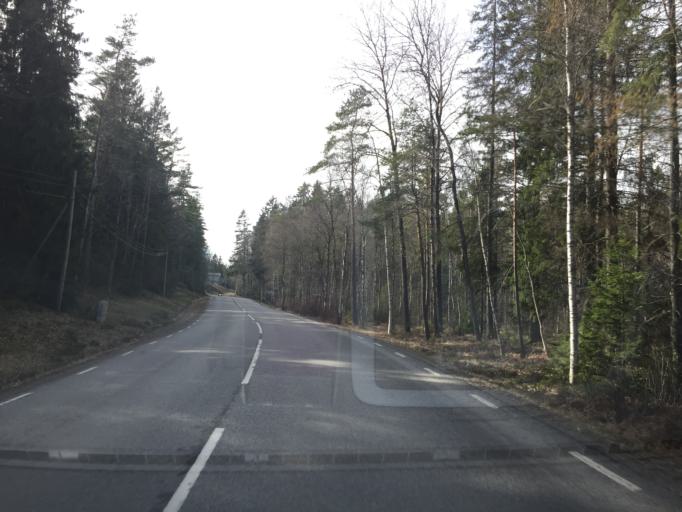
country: SE
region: Stockholm
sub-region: Haninge Kommun
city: Jordbro
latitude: 59.1114
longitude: 18.0009
